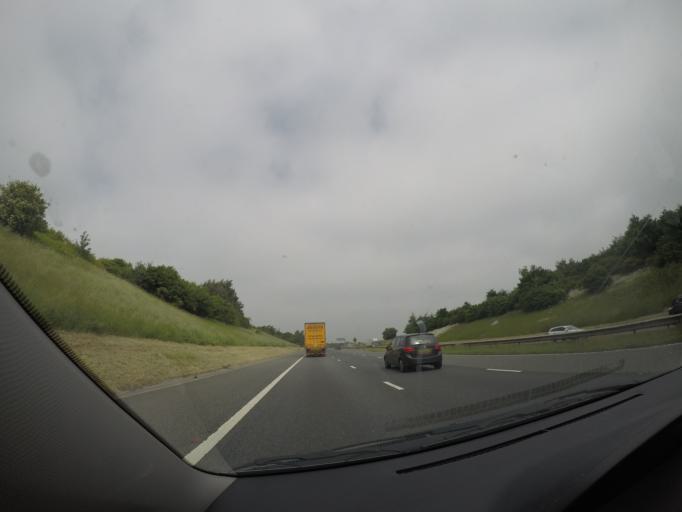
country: GB
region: England
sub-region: North Yorkshire
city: Boroughbridge
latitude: 54.0502
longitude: -1.3887
